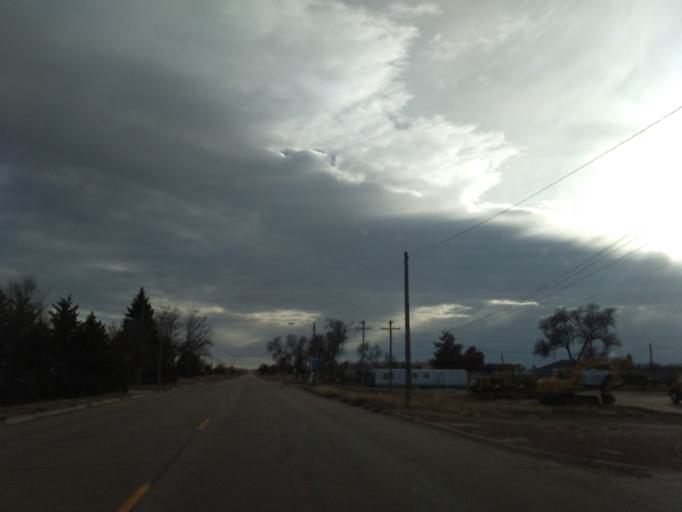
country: US
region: Nebraska
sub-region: Morrill County
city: Bridgeport
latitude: 41.6568
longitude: -103.0995
